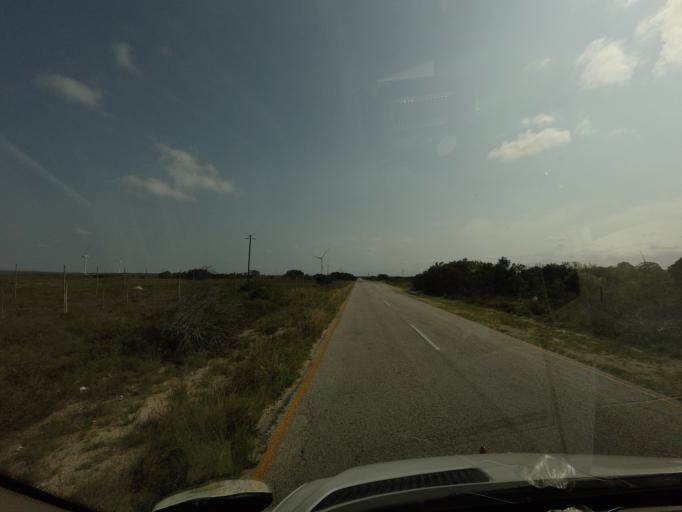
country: ZA
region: Eastern Cape
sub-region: Nelson Mandela Bay Metropolitan Municipality
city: Uitenhage
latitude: -33.6811
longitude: 25.5895
